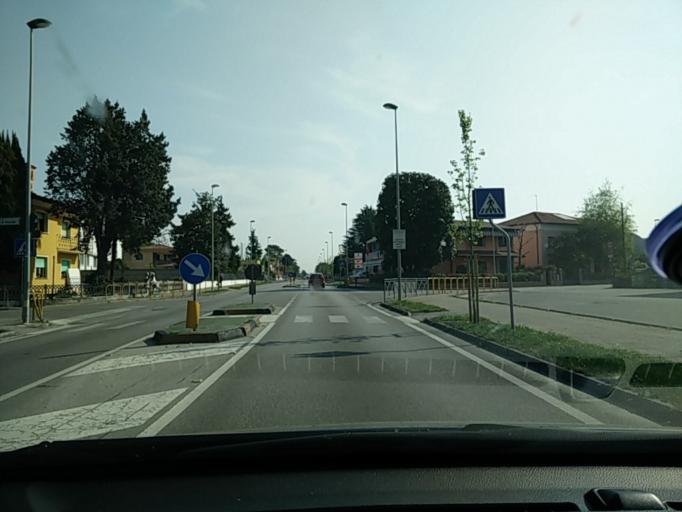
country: IT
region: Friuli Venezia Giulia
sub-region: Provincia di Pordenone
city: Prata di Pordenone
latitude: 45.8930
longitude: 12.5923
